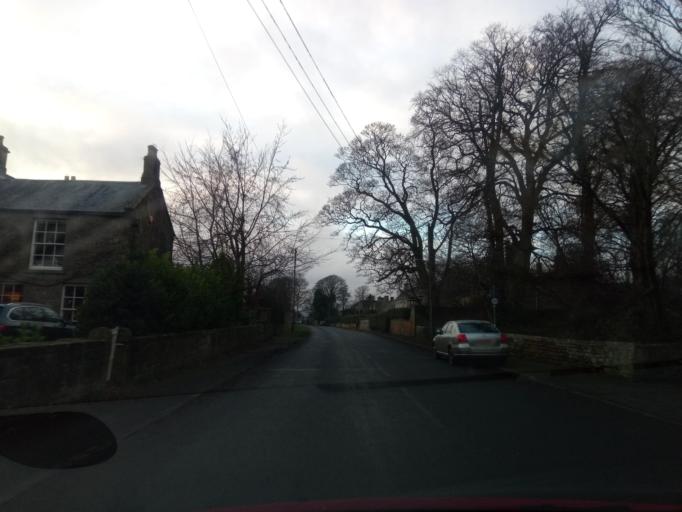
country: GB
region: England
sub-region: Northumberland
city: Meldon
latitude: 55.1269
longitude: -1.7926
